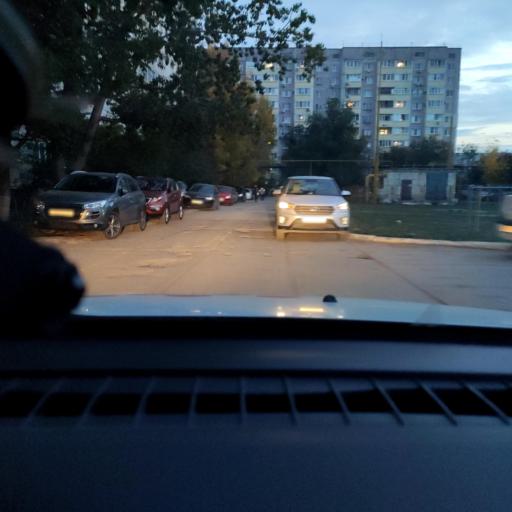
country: RU
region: Samara
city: Samara
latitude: 53.1060
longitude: 50.0822
